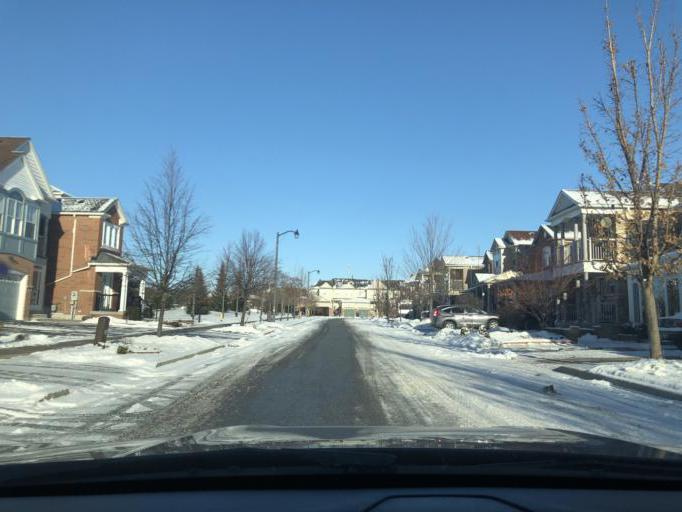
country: CA
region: Ontario
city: Scarborough
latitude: 43.7777
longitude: -79.1375
